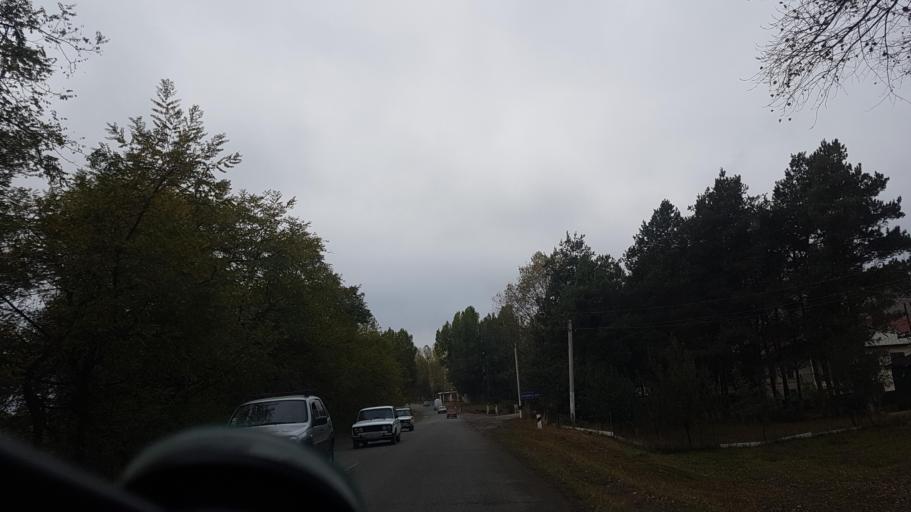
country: AZ
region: Gadabay Rayon
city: Ariqdam
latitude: 40.6357
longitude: 45.8130
